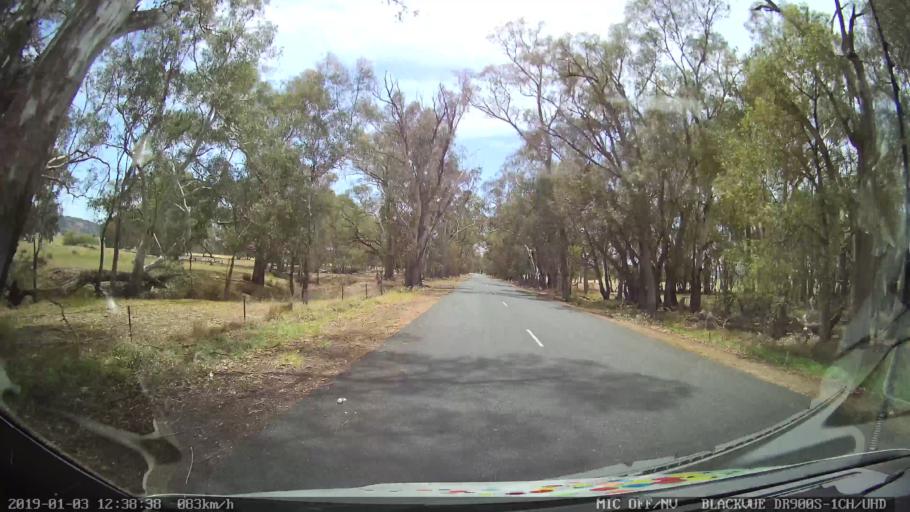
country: AU
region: New South Wales
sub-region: Weddin
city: Grenfell
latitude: -33.8318
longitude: 148.1980
